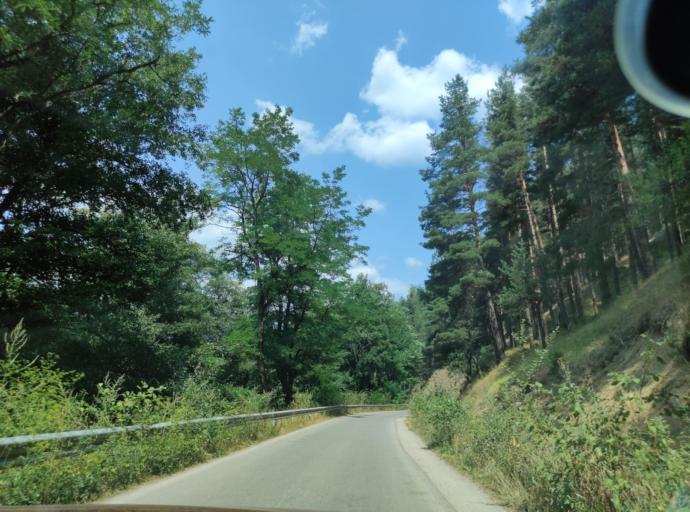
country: BG
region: Blagoevgrad
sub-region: Obshtina Belitsa
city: Belitsa
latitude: 41.9650
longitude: 23.5557
